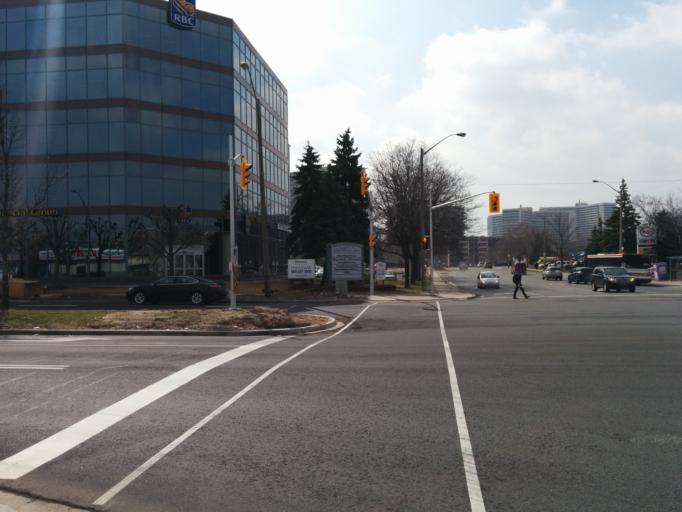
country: CA
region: Ontario
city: Toronto
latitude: 43.7075
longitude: -79.3435
